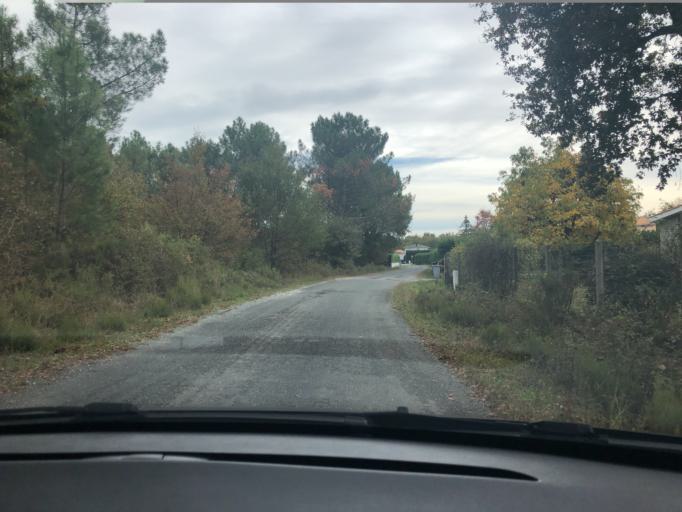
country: FR
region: Aquitaine
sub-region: Departement de la Gironde
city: Le Pian-Medoc
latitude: 44.9491
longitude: -0.6499
